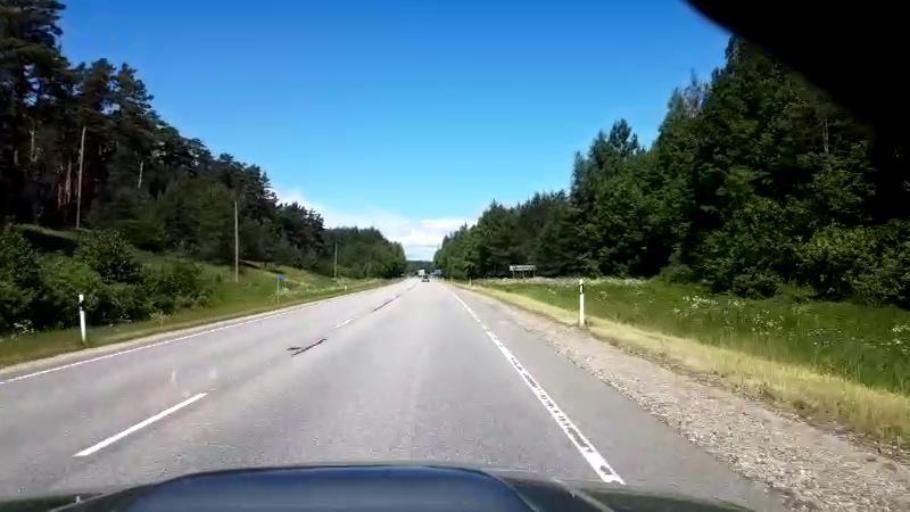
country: LV
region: Salacgrivas
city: Ainazi
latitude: 58.0834
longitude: 24.5098
